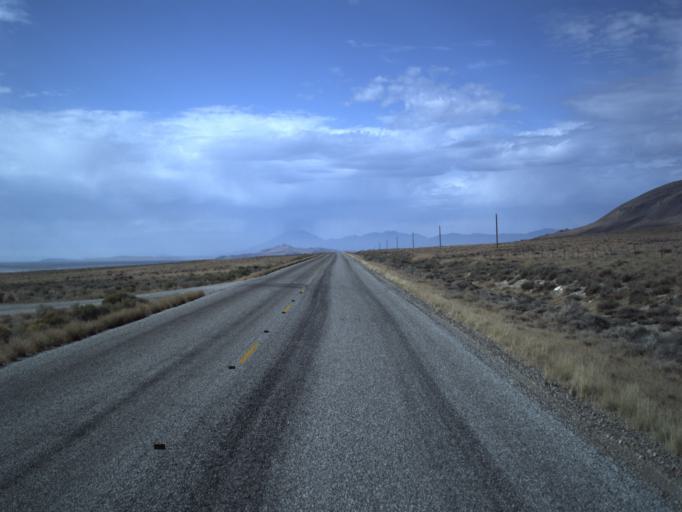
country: US
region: Utah
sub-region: Tooele County
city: Wendover
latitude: 41.4964
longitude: -113.6125
